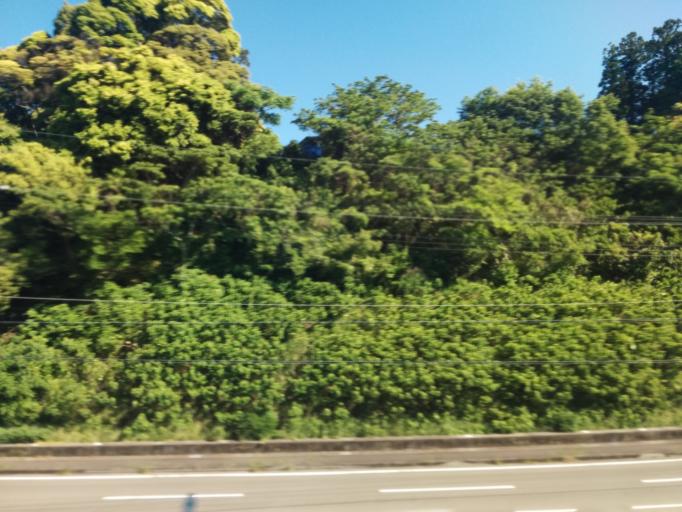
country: JP
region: Shizuoka
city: Shimada
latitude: 34.8019
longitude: 138.1991
